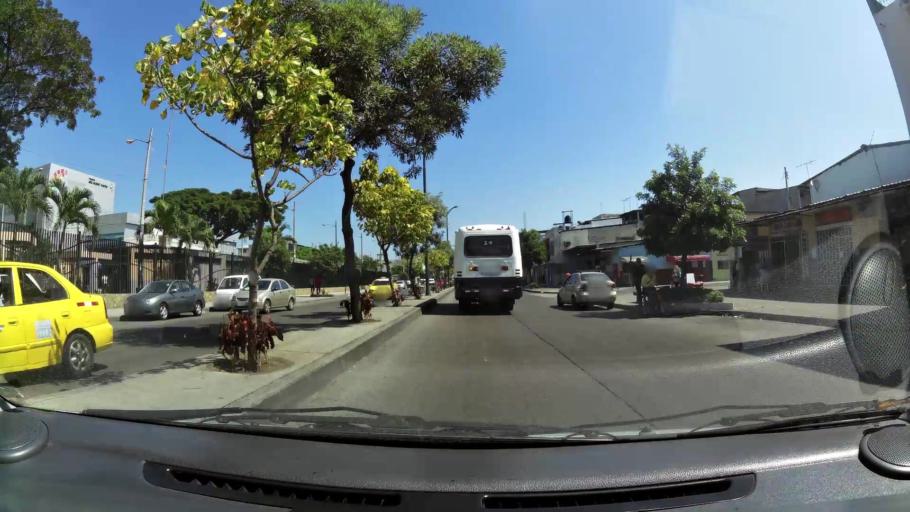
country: EC
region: Guayas
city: Guayaquil
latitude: -2.2112
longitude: -79.9311
